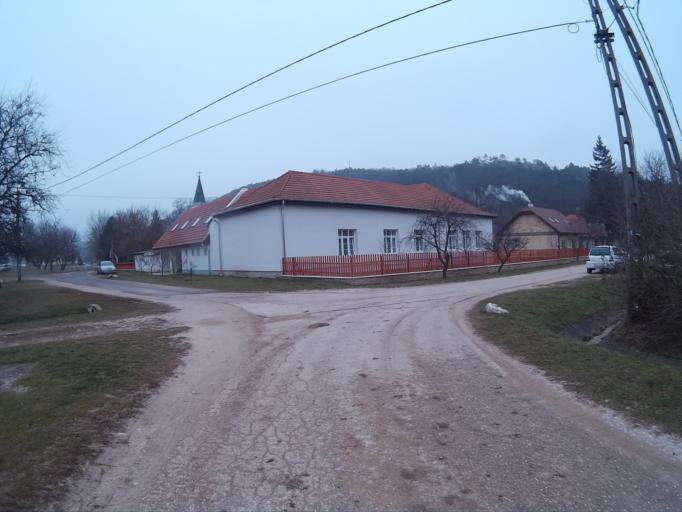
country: HU
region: Fejer
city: Zamoly
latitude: 47.3905
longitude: 18.3861
